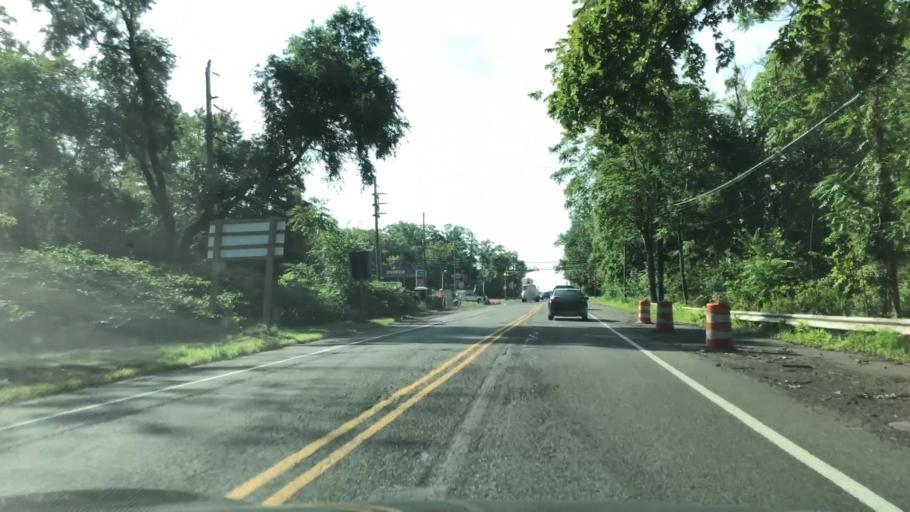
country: US
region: New Jersey
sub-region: Mercer County
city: Pennington
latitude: 40.3155
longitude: -74.7936
